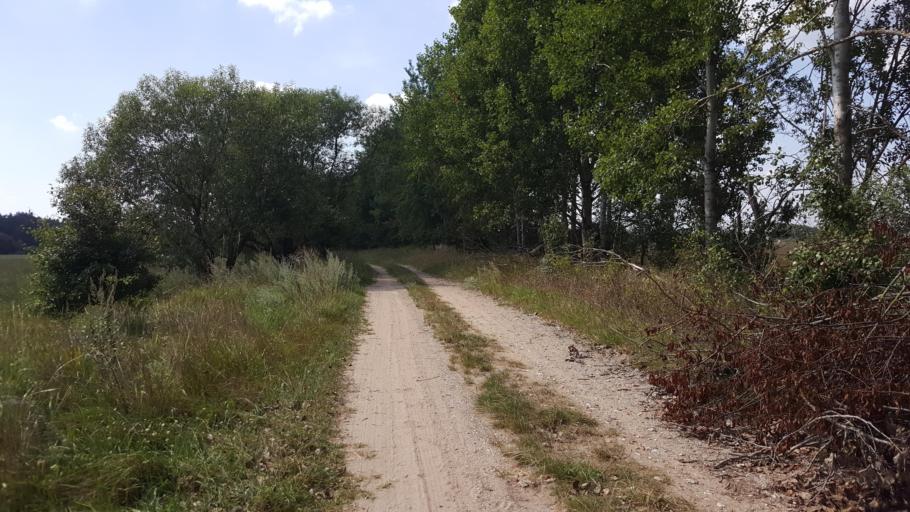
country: PL
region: Podlasie
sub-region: Powiat hajnowski
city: Hajnowka
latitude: 52.5764
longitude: 23.5684
